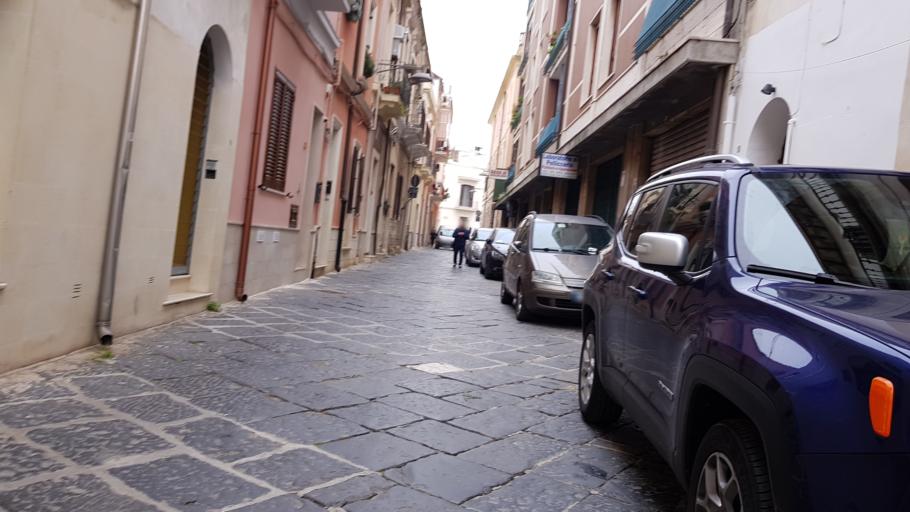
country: IT
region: Apulia
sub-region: Provincia di Brindisi
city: Brindisi
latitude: 40.6370
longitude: 17.9398
